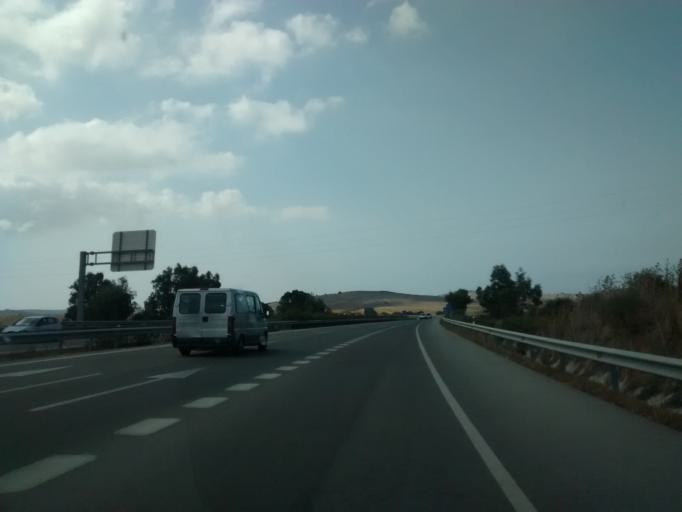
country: ES
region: Andalusia
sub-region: Provincia de Cadiz
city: Conil de la Frontera
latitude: 36.2680
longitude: -6.0285
